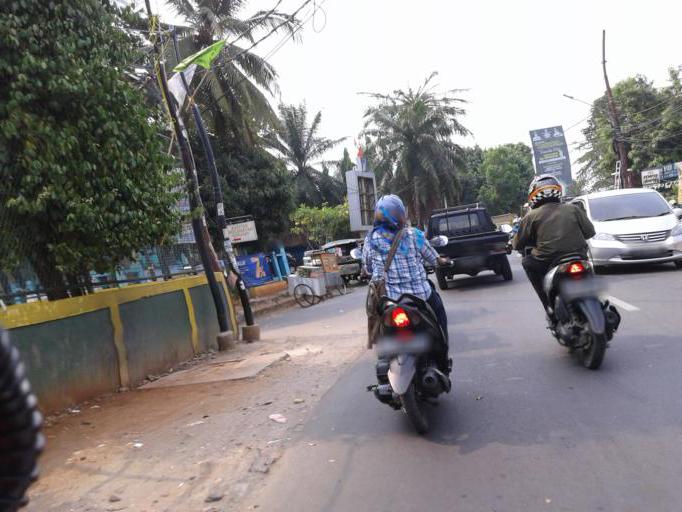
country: ID
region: Banten
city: South Tangerang
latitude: -6.2905
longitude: 106.7299
